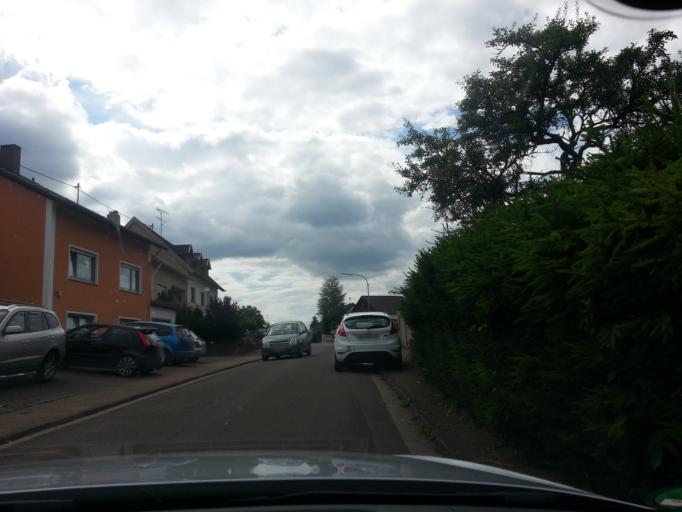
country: DE
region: Saarland
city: Nalbach
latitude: 49.4125
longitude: 6.7716
